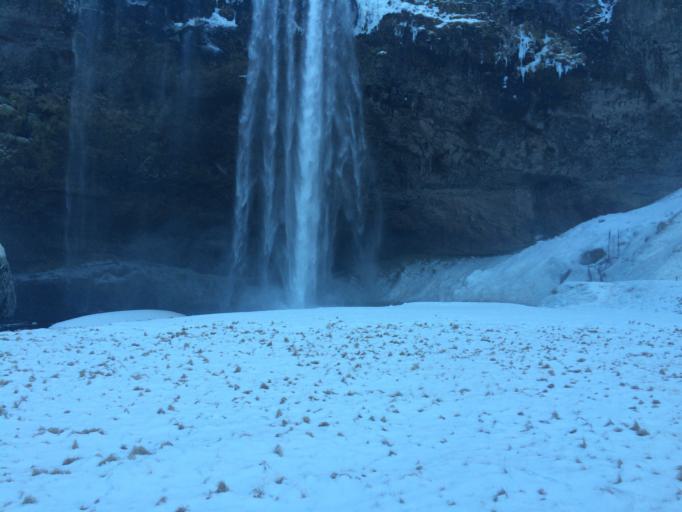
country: IS
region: South
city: Vestmannaeyjar
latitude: 63.6159
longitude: -19.9898
